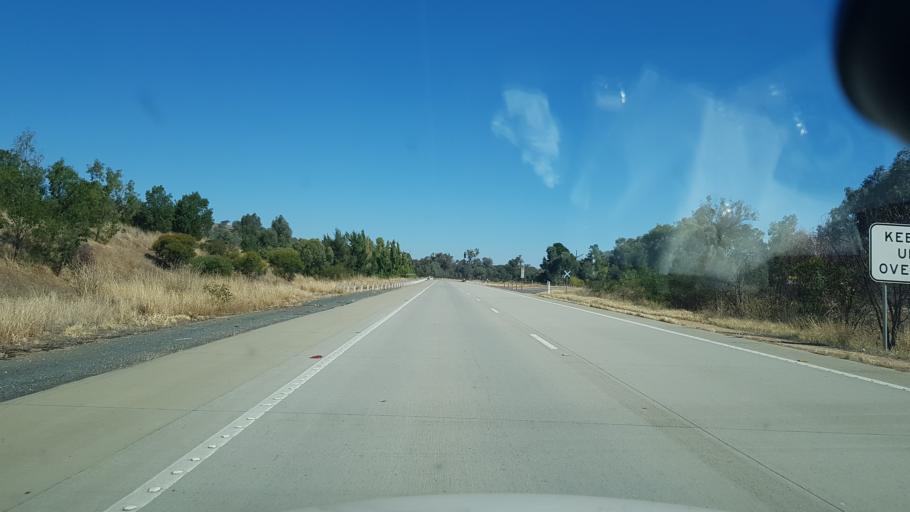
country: AU
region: New South Wales
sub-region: Greater Hume Shire
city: Holbrook
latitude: -35.8989
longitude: 147.1660
